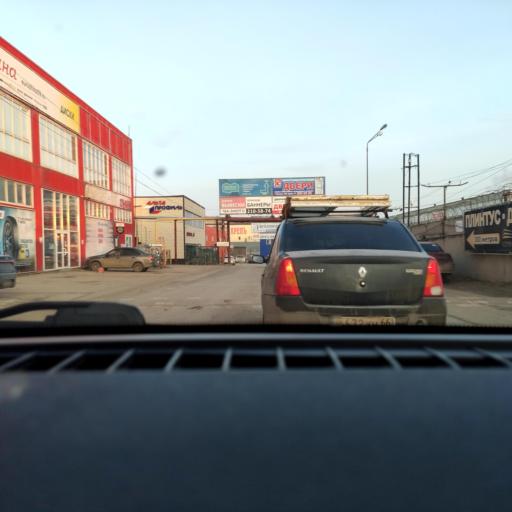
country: RU
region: Perm
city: Froly
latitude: 57.9579
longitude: 56.2766
